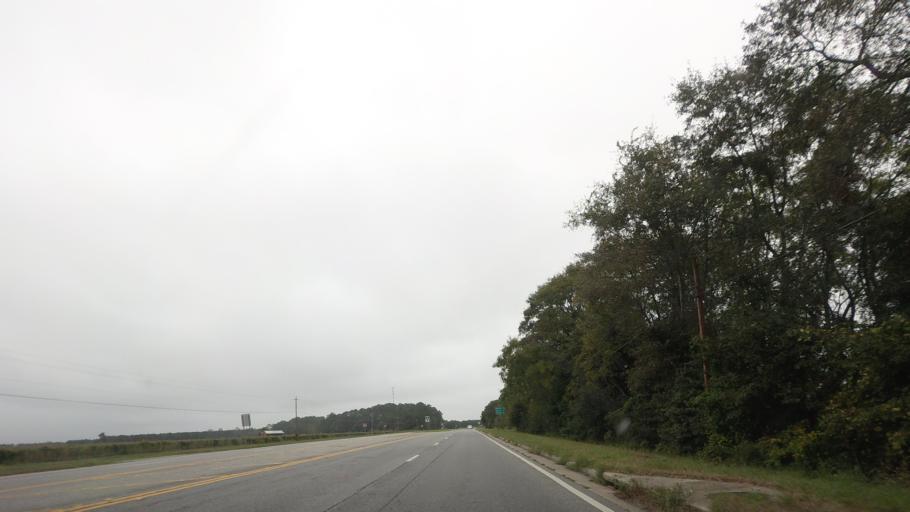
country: US
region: Georgia
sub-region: Berrien County
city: Enigma
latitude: 31.3909
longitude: -83.2311
